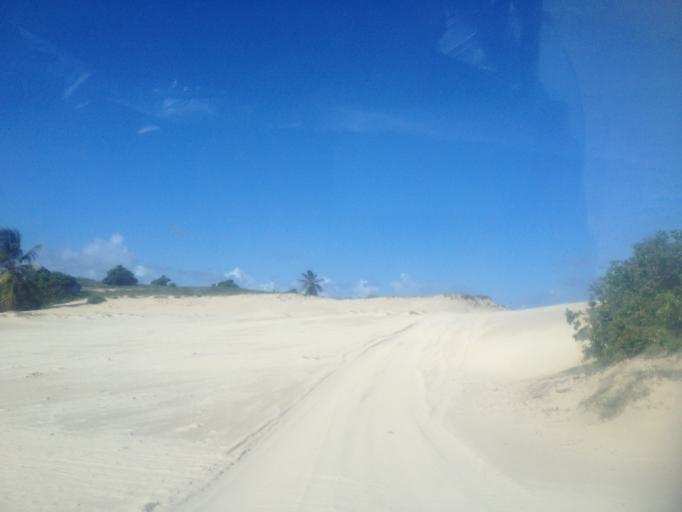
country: BR
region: Sergipe
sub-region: Indiaroba
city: Indiaroba
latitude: -11.4691
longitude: -37.3702
